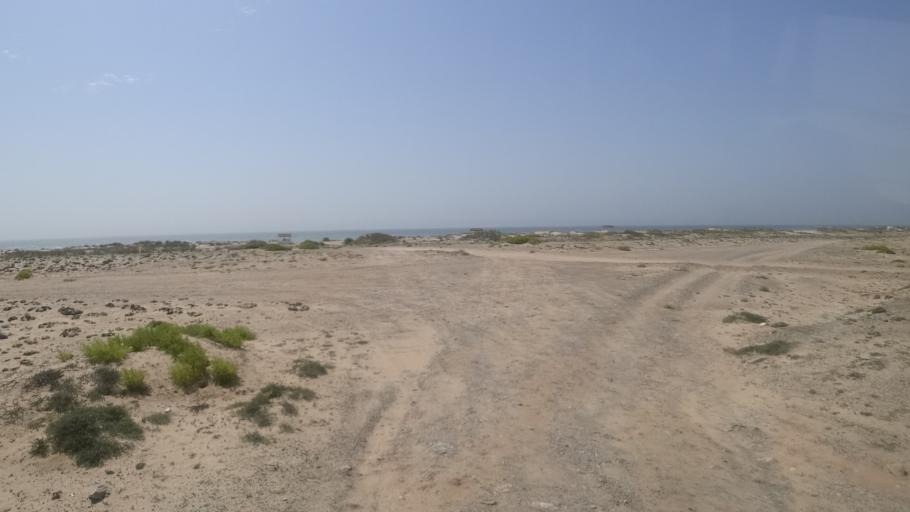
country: OM
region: Ash Sharqiyah
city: Sur
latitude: 22.1056
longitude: 59.7066
